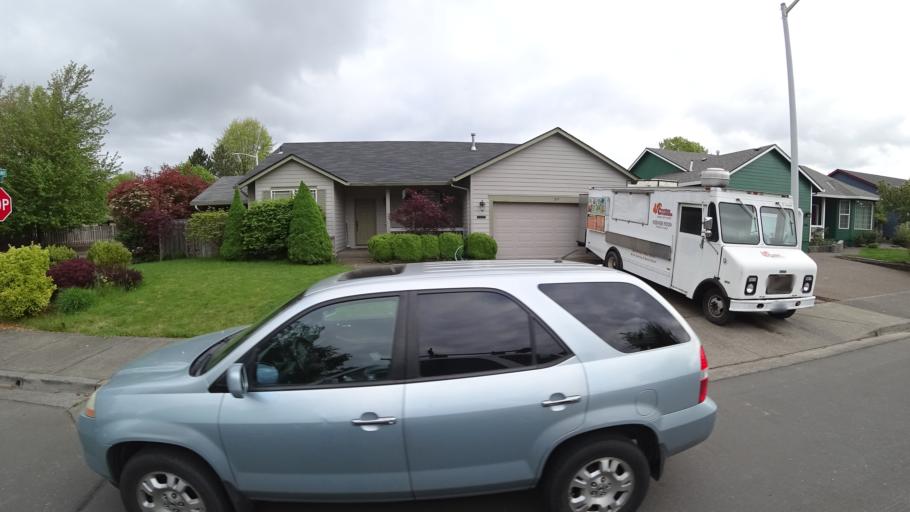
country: US
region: Oregon
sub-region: Washington County
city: Hillsboro
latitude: 45.5339
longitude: -122.9605
